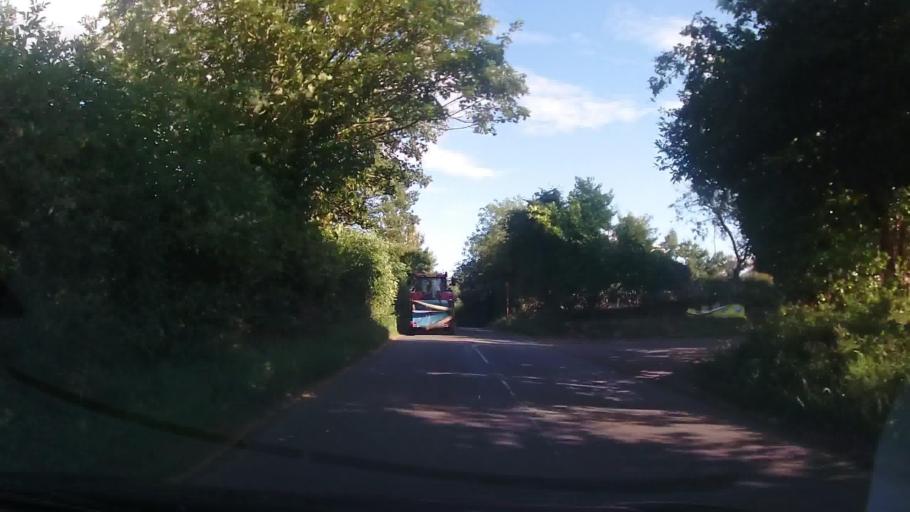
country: GB
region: England
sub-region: Shropshire
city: Great Hanwood
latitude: 52.6510
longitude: -2.7997
